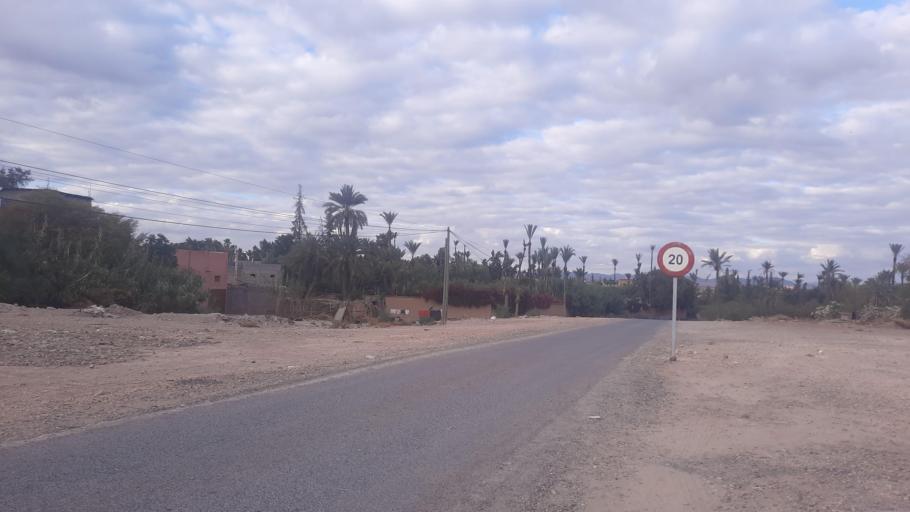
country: MA
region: Marrakech-Tensift-Al Haouz
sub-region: Marrakech
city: Marrakesh
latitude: 31.6724
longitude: -7.9540
